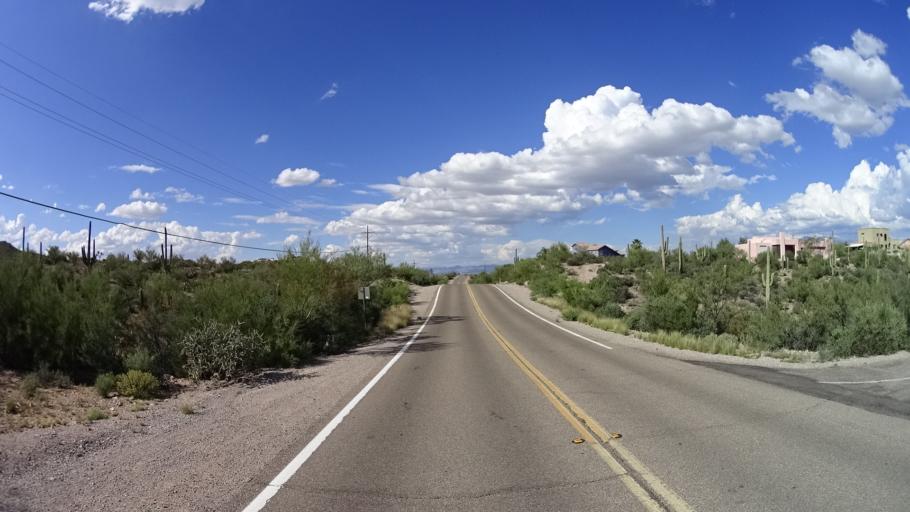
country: US
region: Arizona
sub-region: Pima County
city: Tucson Estates
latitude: 32.2468
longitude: -111.0628
